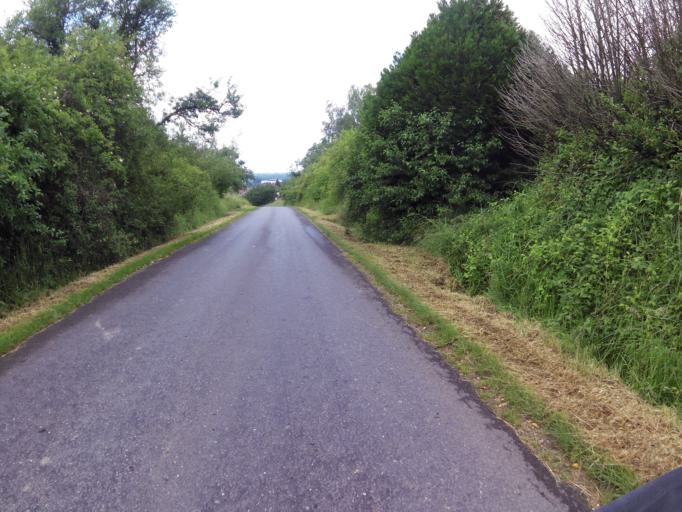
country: FR
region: Champagne-Ardenne
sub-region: Departement de la Marne
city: Sermaize-les-Bains
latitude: 48.7784
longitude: 4.9197
